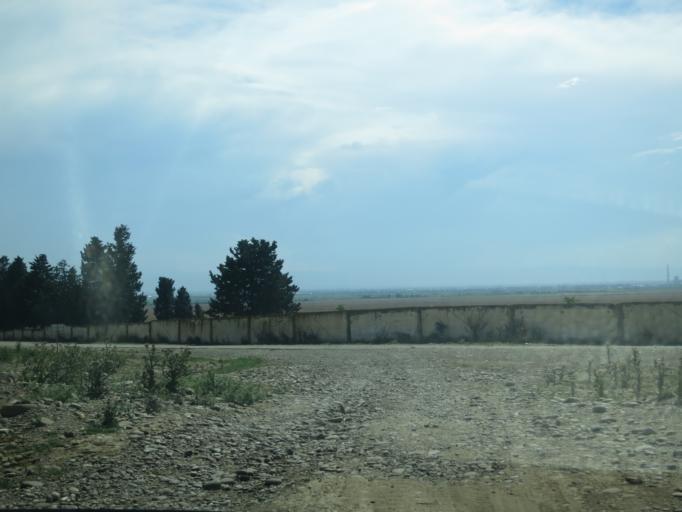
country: GE
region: Kvemo Kartli
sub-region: Gardabani
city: Gardabani
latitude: 41.5019
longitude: 45.1909
